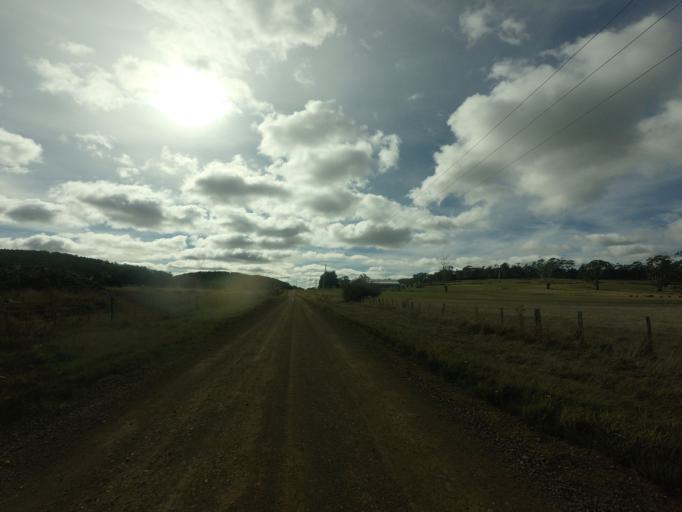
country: AU
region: Tasmania
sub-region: Brighton
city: Bridgewater
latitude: -42.4012
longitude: 147.3910
